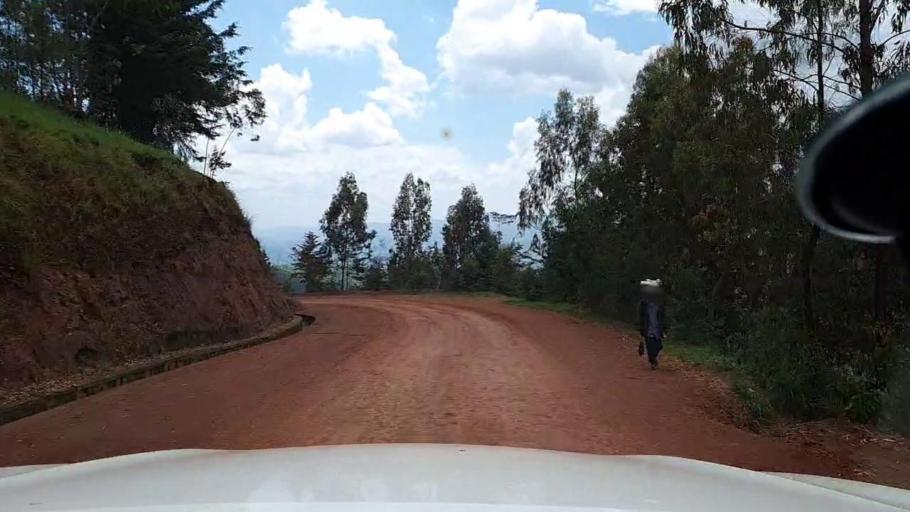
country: RW
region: Kigali
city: Kigali
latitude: -1.7990
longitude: 29.8435
